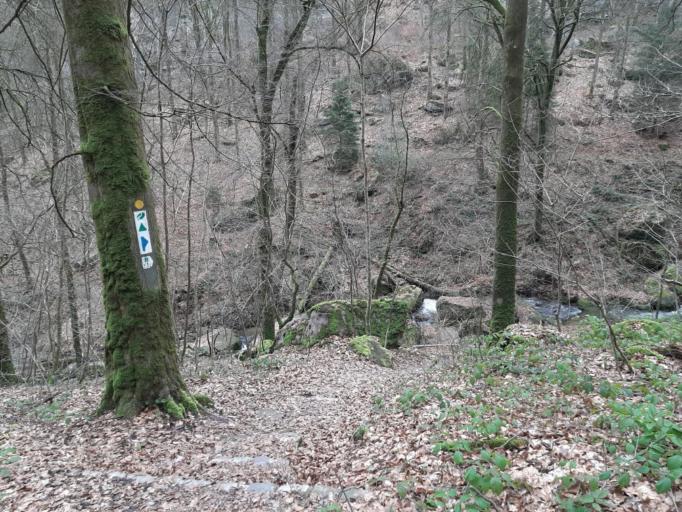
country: LU
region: Grevenmacher
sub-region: Canton d'Echternach
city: Beaufort
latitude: 49.8232
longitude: 6.3114
